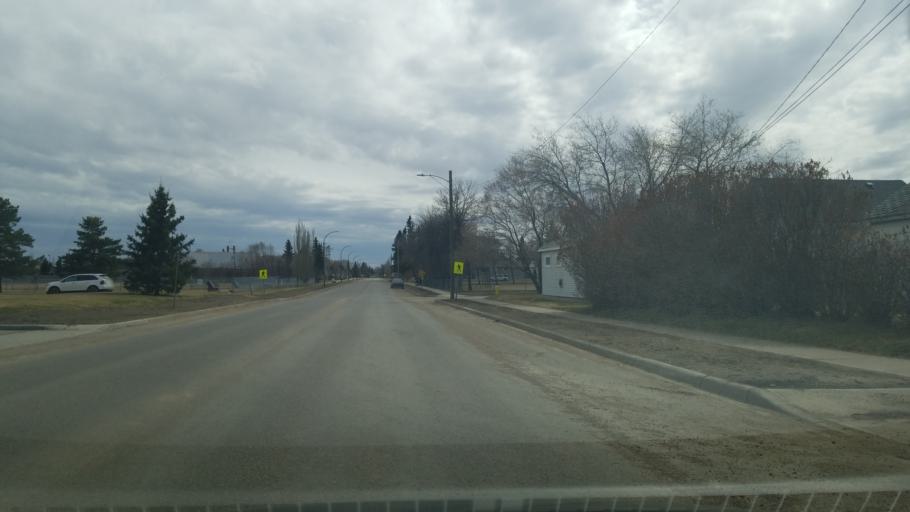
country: CA
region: Saskatchewan
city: Lloydminster
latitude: 53.2766
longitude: -109.9975
